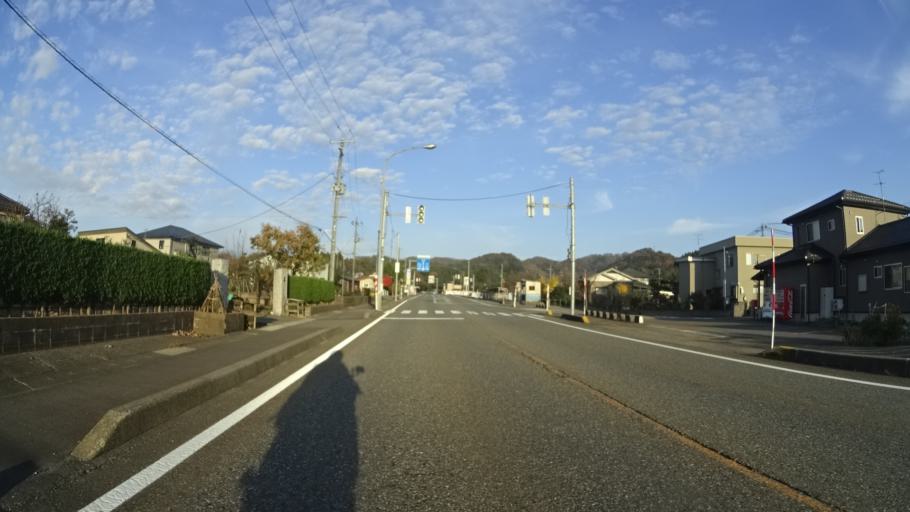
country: JP
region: Niigata
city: Kashiwazaki
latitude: 37.4040
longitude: 138.6360
